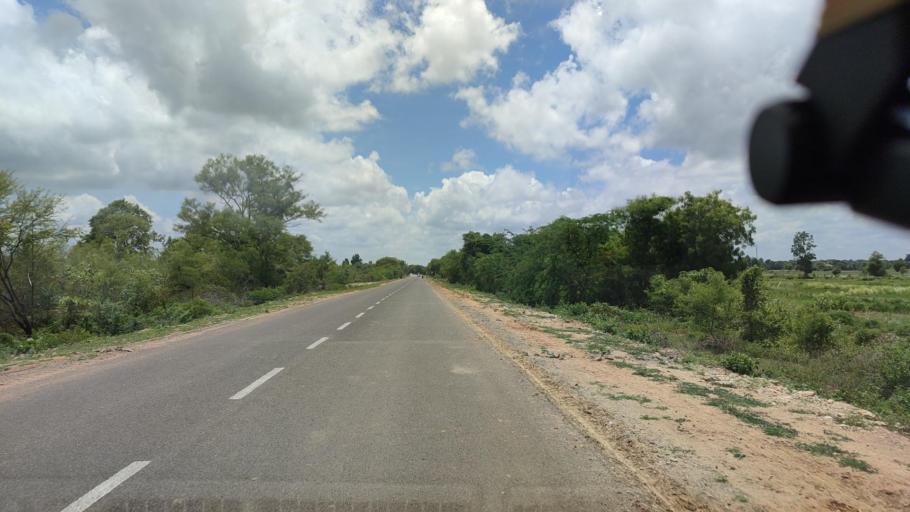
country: MM
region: Magway
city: Taungdwingyi
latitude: 20.1832
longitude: 95.4573
